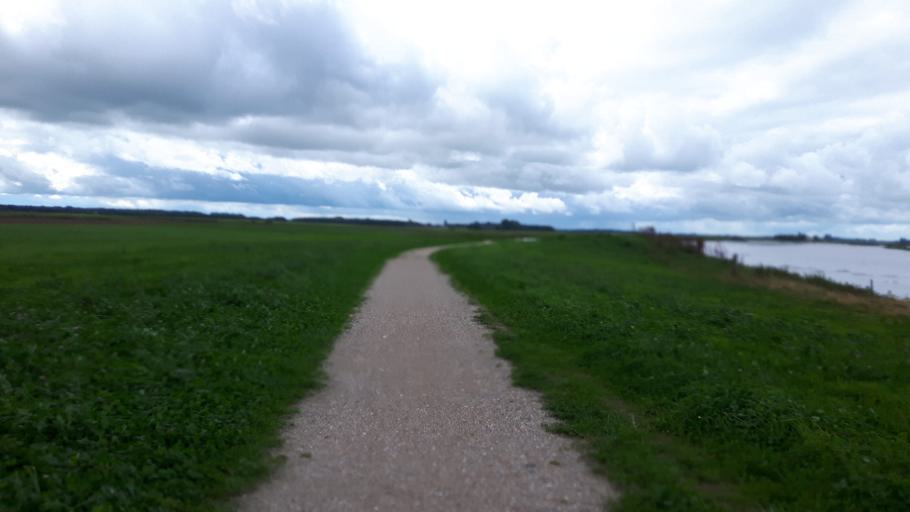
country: NL
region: Groningen
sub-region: Gemeente Slochteren
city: Slochteren
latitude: 53.2473
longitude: 6.7932
